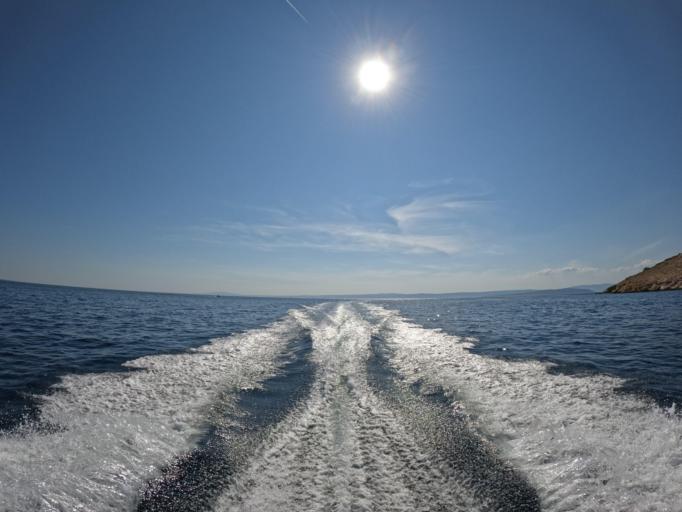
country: HR
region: Primorsko-Goranska
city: Punat
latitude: 44.9629
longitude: 14.6568
